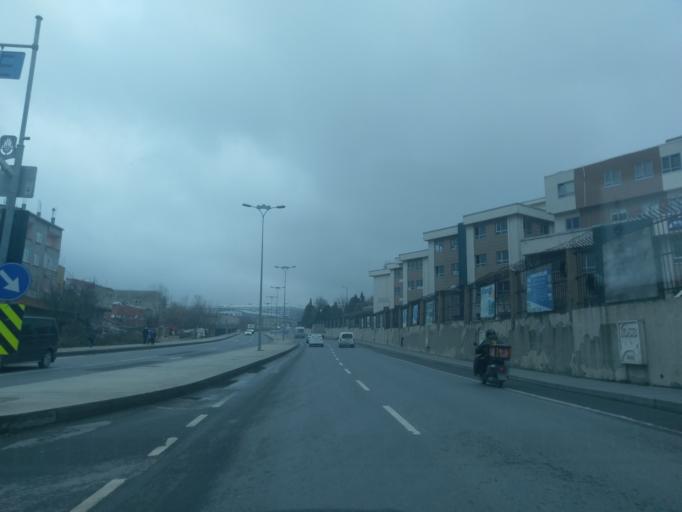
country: TR
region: Istanbul
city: Basaksehir
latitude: 41.0739
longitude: 28.7936
